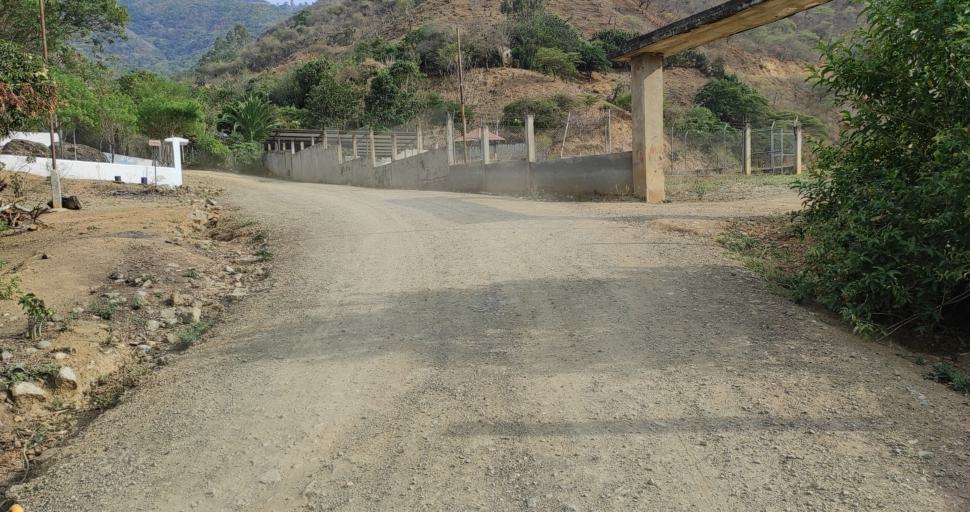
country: EC
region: Loja
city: Catacocha
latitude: -3.9922
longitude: -79.6981
